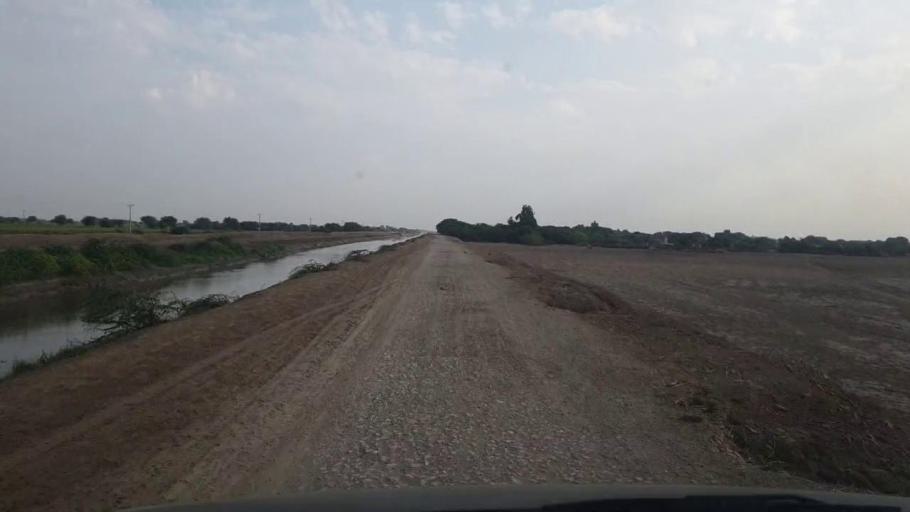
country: PK
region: Sindh
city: Badin
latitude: 24.5267
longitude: 68.6799
